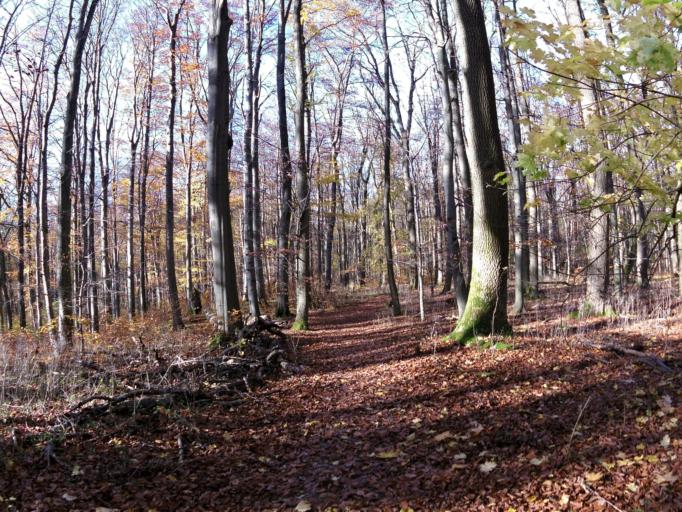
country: DE
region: Thuringia
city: Weberstedt
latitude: 51.0711
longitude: 10.4524
